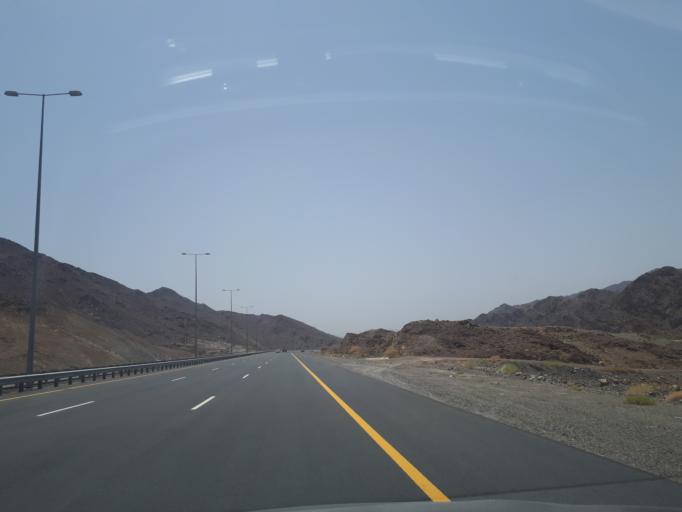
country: OM
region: Ash Sharqiyah
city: Ibra'
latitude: 22.8848
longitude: 58.2929
